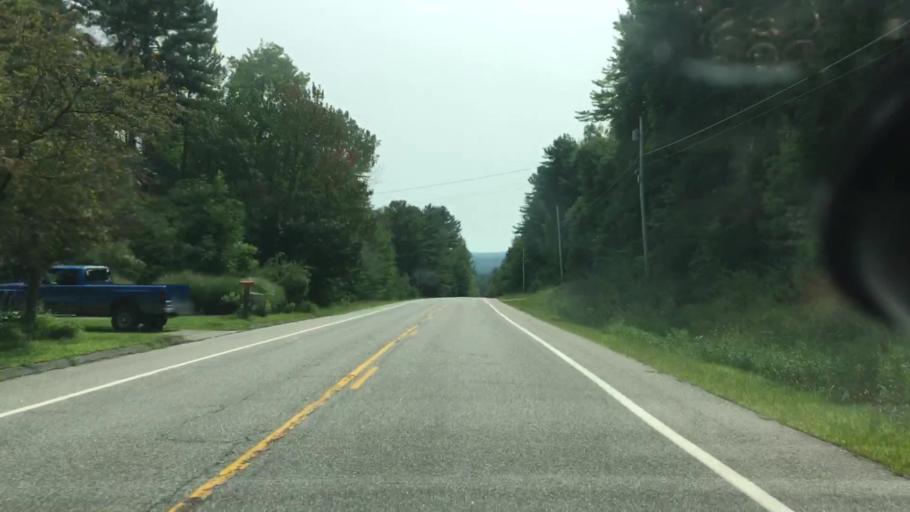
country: US
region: Maine
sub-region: Kennebec County
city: Wayne
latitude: 44.3754
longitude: -70.0976
